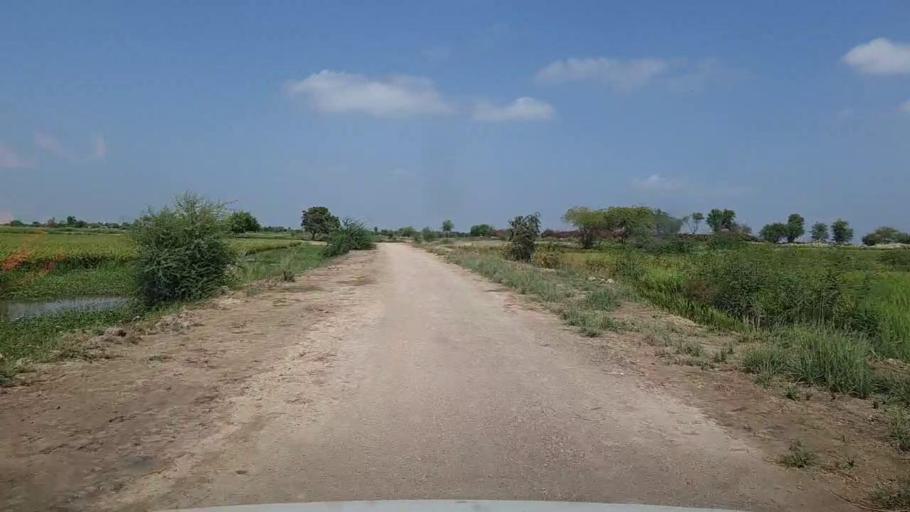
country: PK
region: Sindh
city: Kario
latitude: 24.6859
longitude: 68.6015
